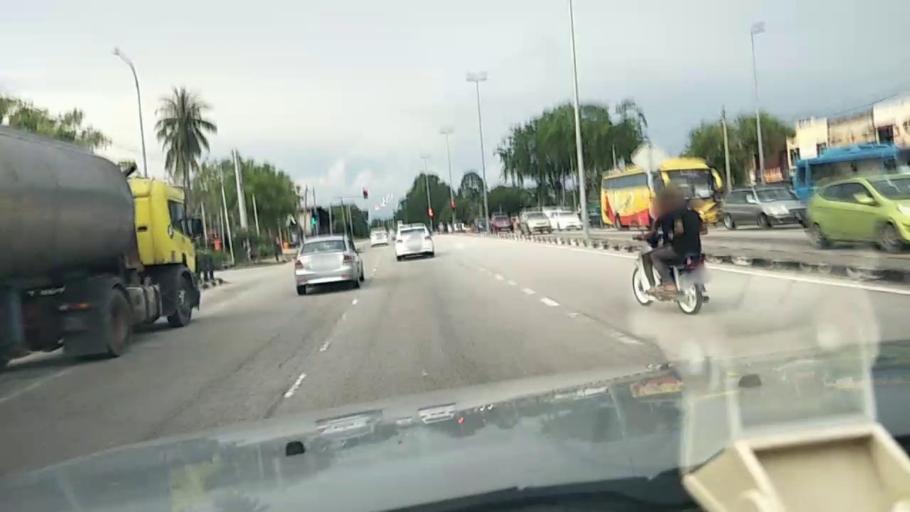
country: MY
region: Perak
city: Kampong Dungun
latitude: 3.1324
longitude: 101.3756
